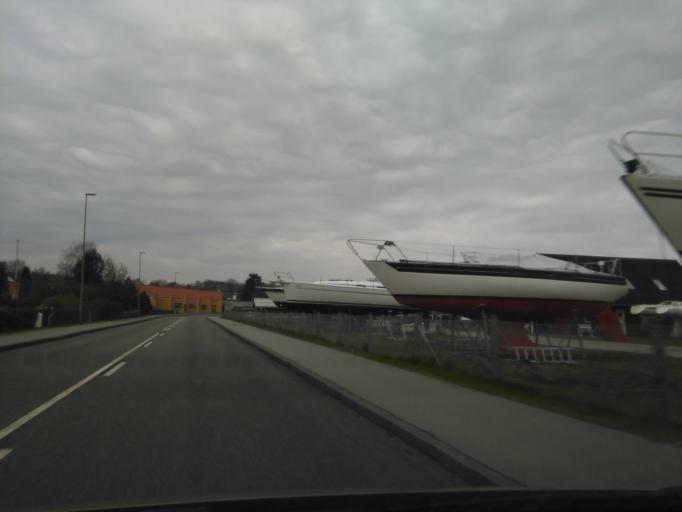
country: DK
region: North Denmark
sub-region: Mariagerfjord Kommune
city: Mariager
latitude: 56.6535
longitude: 9.9842
